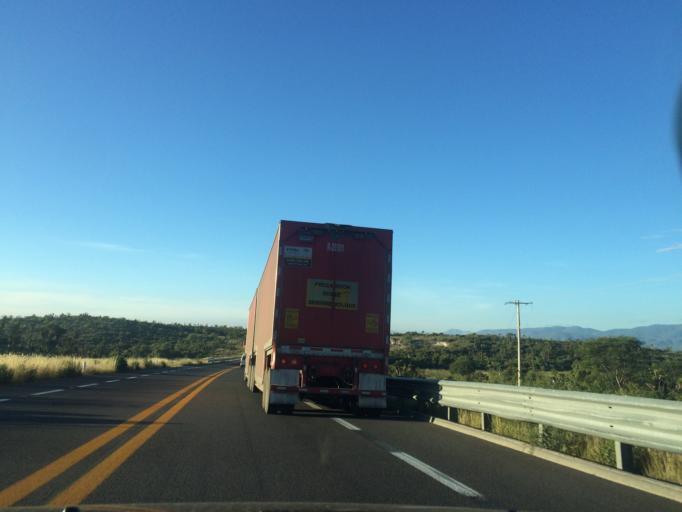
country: MX
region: Puebla
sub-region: Tehuacan
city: Magdalena Cuayucatepec
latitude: 18.5809
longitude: -97.4659
